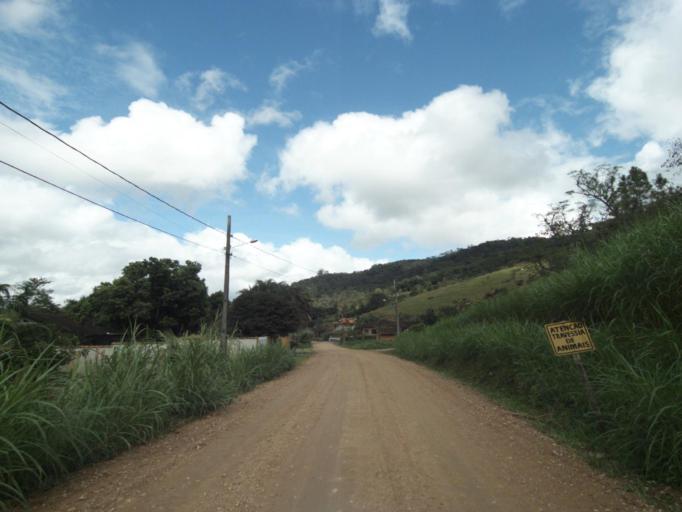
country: BR
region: Santa Catarina
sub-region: Pomerode
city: Pomerode
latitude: -26.6760
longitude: -49.1871
